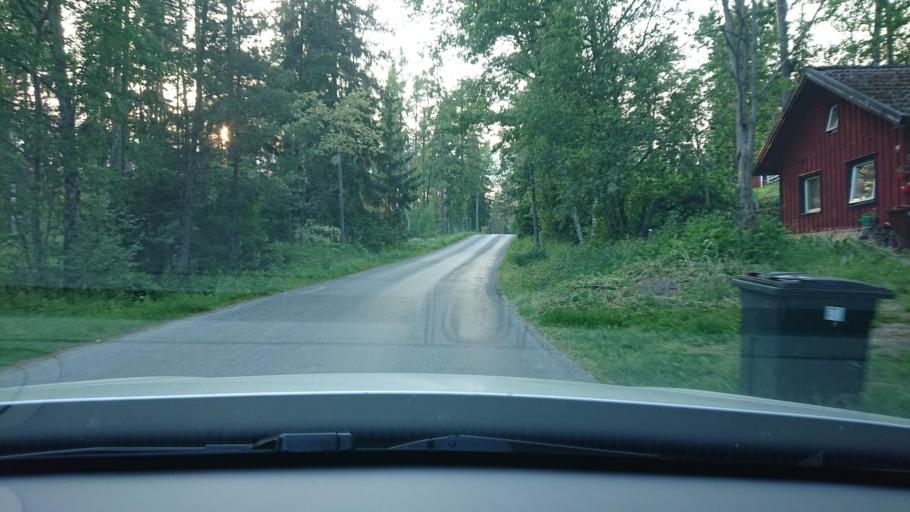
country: SE
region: Stockholm
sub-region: Osterakers Kommun
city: Akersberga
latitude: 59.5035
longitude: 18.3396
